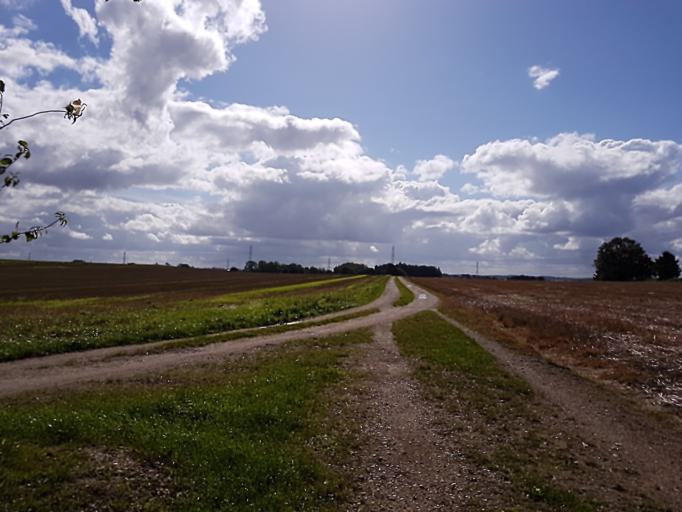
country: DK
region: Zealand
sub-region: Roskilde Kommune
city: Jyllinge
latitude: 55.7887
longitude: 12.1027
